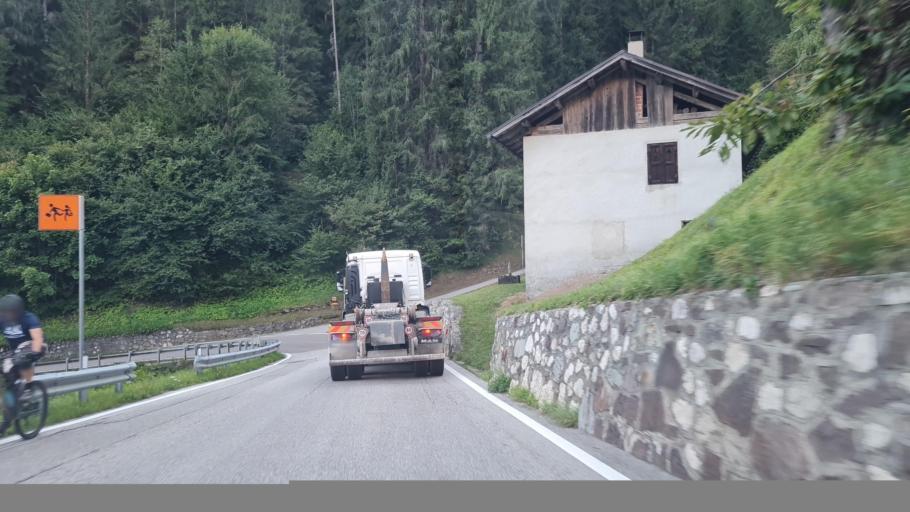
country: IT
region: Trentino-Alto Adige
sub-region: Provincia di Trento
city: Siror
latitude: 46.2047
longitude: 11.8189
